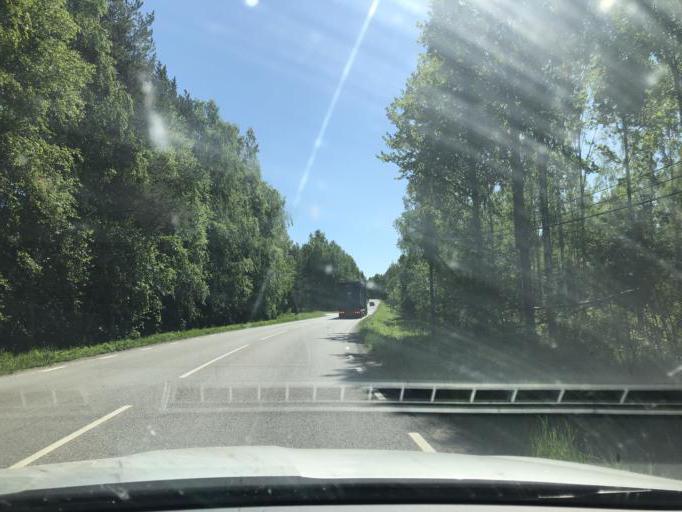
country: SE
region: Norrbotten
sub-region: Lulea Kommun
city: Sodra Sunderbyn
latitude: 65.6642
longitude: 21.9683
